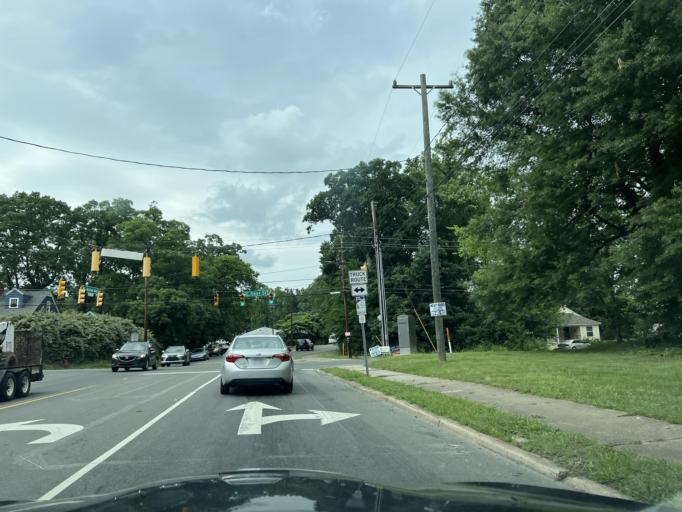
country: US
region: North Carolina
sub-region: Durham County
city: Durham
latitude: 36.0033
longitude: -78.8860
